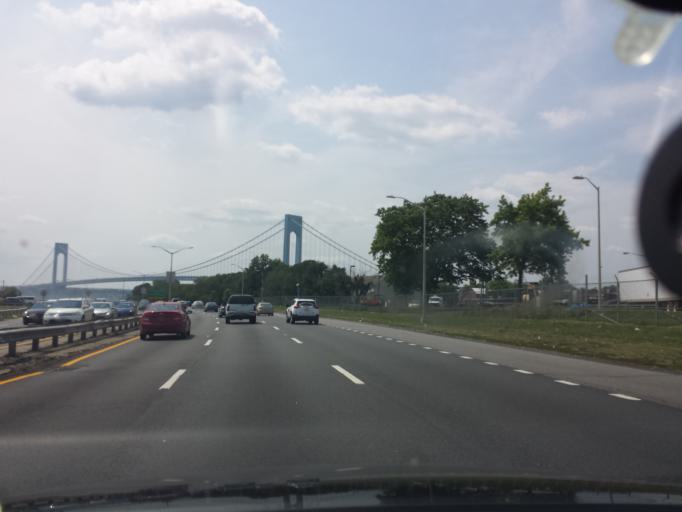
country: US
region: New York
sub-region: Kings County
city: Bensonhurst
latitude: 40.6048
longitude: -74.0224
